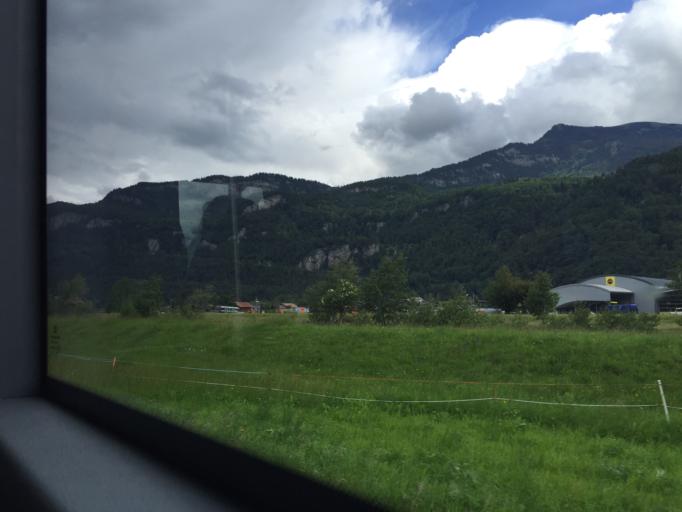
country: CH
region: Bern
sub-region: Interlaken-Oberhasli District
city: Meiringen
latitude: 46.7282
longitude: 8.1686
